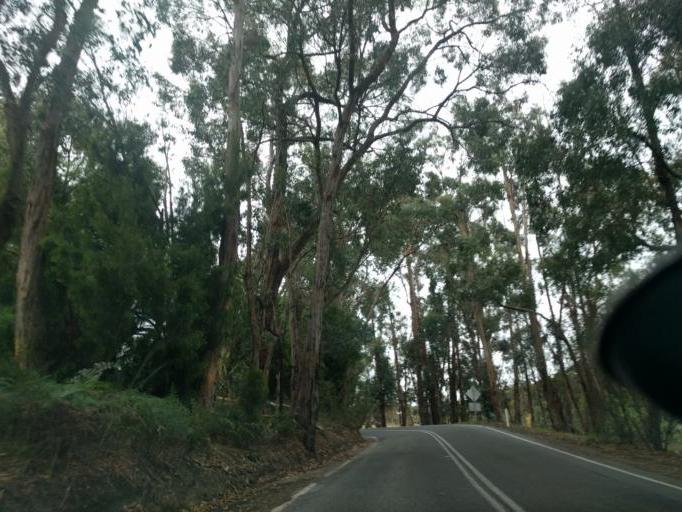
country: AU
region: South Australia
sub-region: Adelaide Hills
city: Stirling
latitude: -35.0326
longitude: 138.7647
